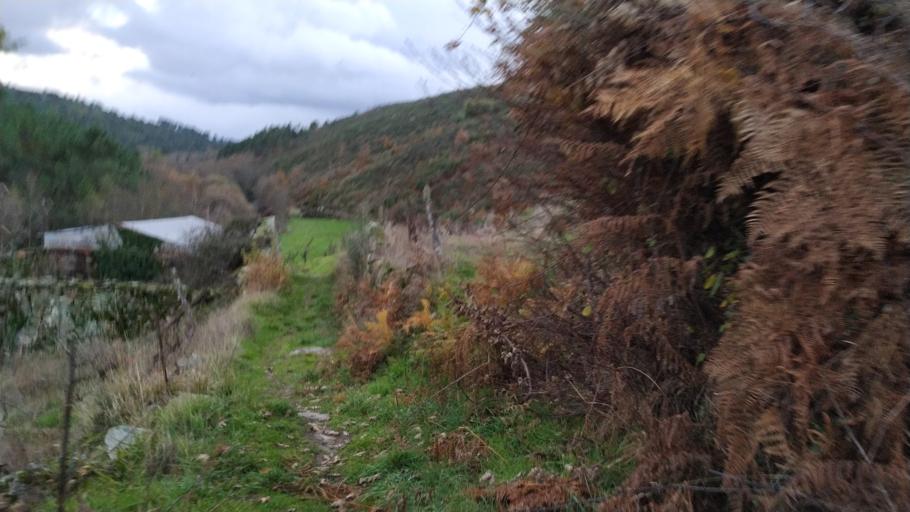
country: PT
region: Vila Real
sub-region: Vila Real
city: Vila Real
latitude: 41.3501
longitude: -7.7129
